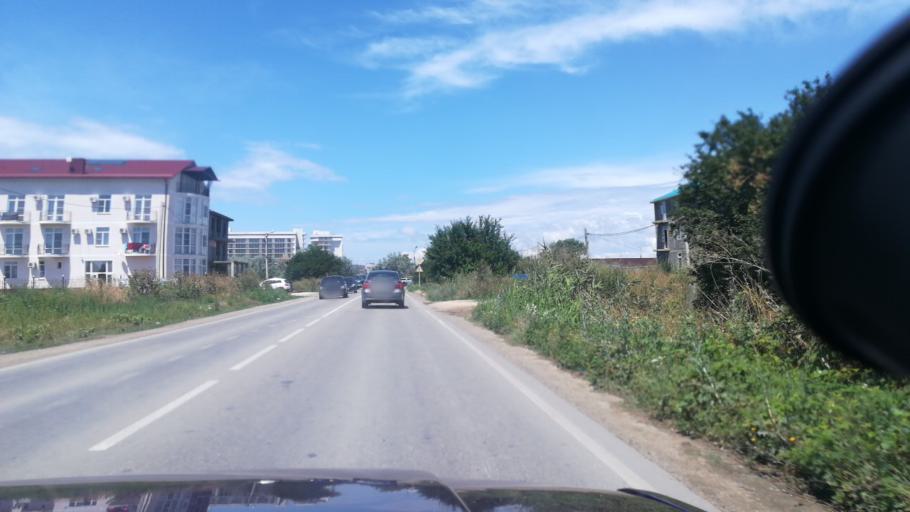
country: RU
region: Krasnodarskiy
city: Vityazevo
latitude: 44.9629
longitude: 37.2921
